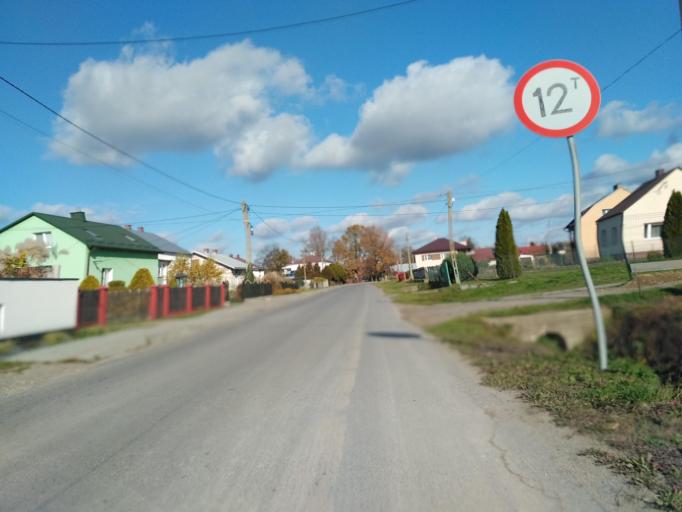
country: PL
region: Subcarpathian Voivodeship
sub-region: Powiat rzeszowski
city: Swilcza
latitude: 50.1332
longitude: 21.9027
